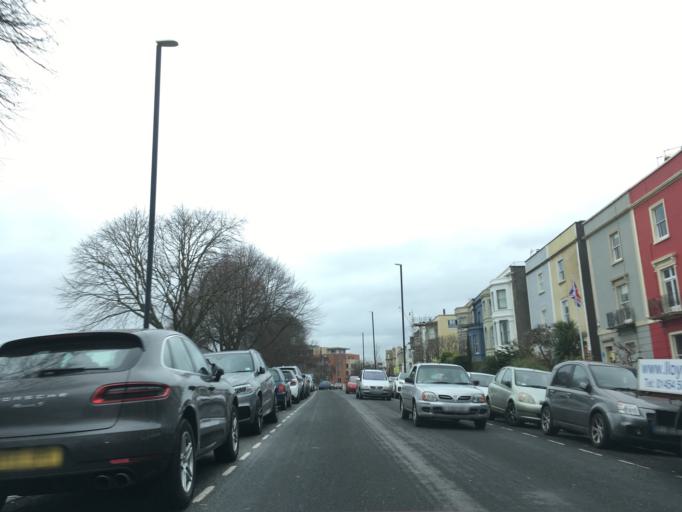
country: GB
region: England
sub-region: Bristol
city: Bristol
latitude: 51.4692
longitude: -2.6188
